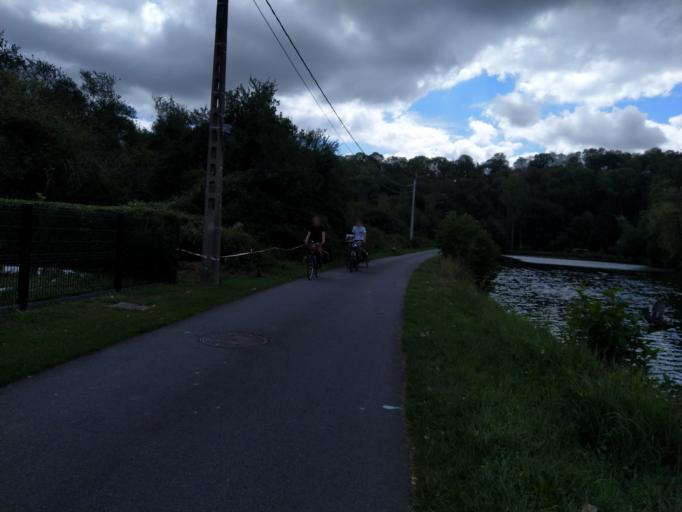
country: BE
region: Wallonia
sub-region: Province du Hainaut
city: Lobbes
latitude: 50.3435
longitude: 4.2691
